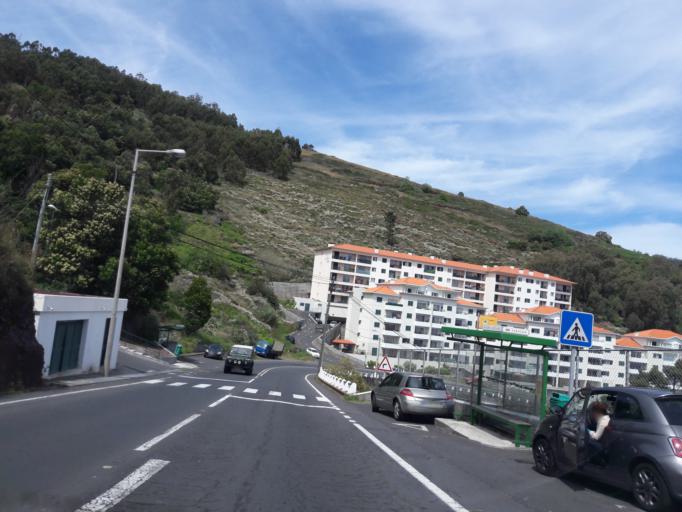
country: PT
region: Madeira
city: Canico
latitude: 32.6526
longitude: -16.8489
